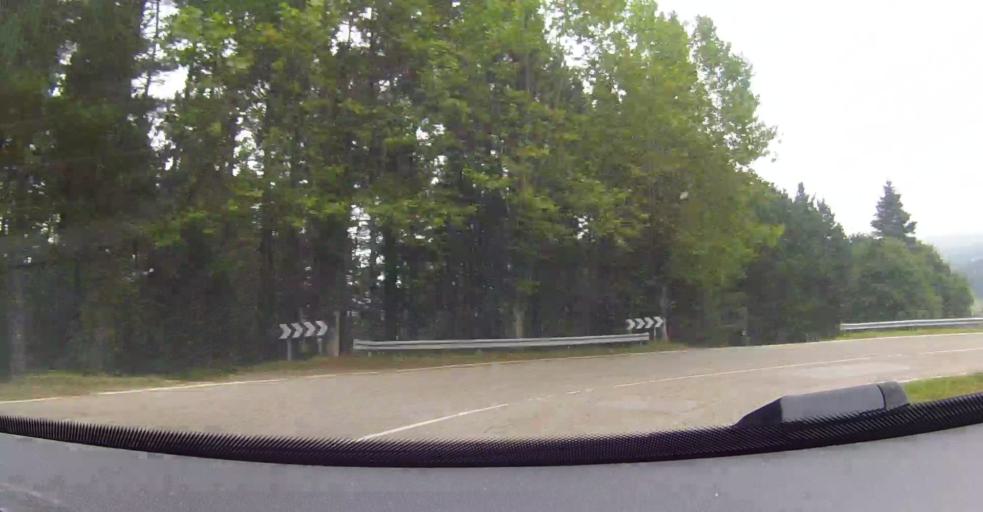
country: ES
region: Basque Country
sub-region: Bizkaia
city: Balmaseda
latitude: 43.2518
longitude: -3.2753
